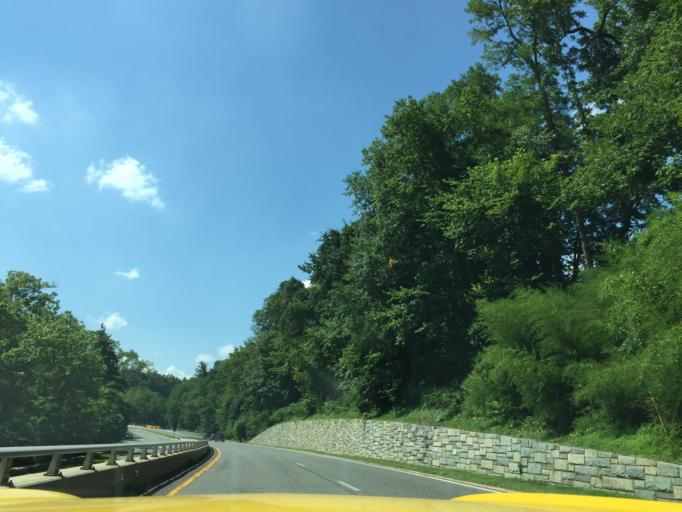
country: US
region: Maryland
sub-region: Montgomery County
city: Cabin John
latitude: 38.9693
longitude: -77.1439
